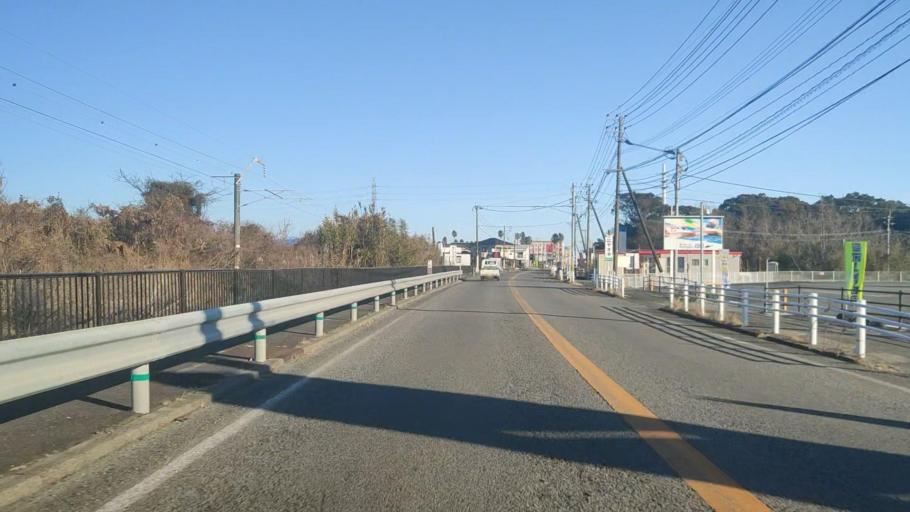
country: JP
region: Miyazaki
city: Nobeoka
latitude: 32.3894
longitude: 131.6275
